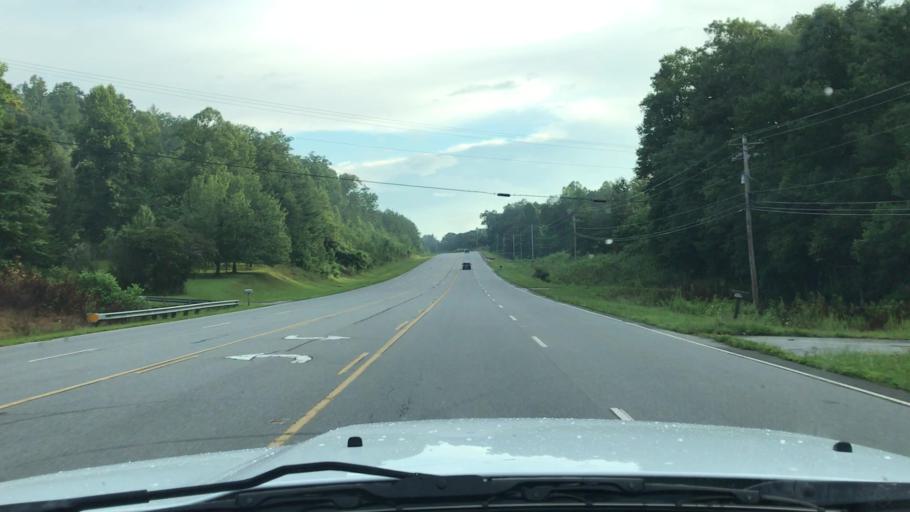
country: US
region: North Carolina
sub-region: Cherokee County
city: Murphy
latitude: 35.0244
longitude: -84.1144
